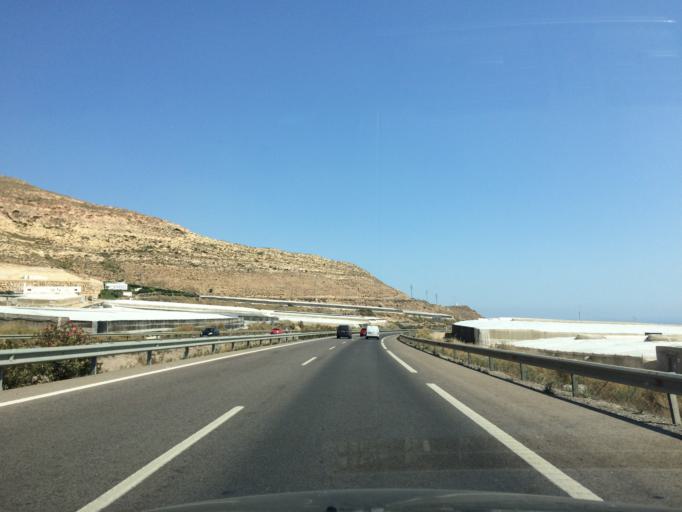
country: ES
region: Andalusia
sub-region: Provincia de Almeria
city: Vicar
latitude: 36.8138
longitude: -2.6450
